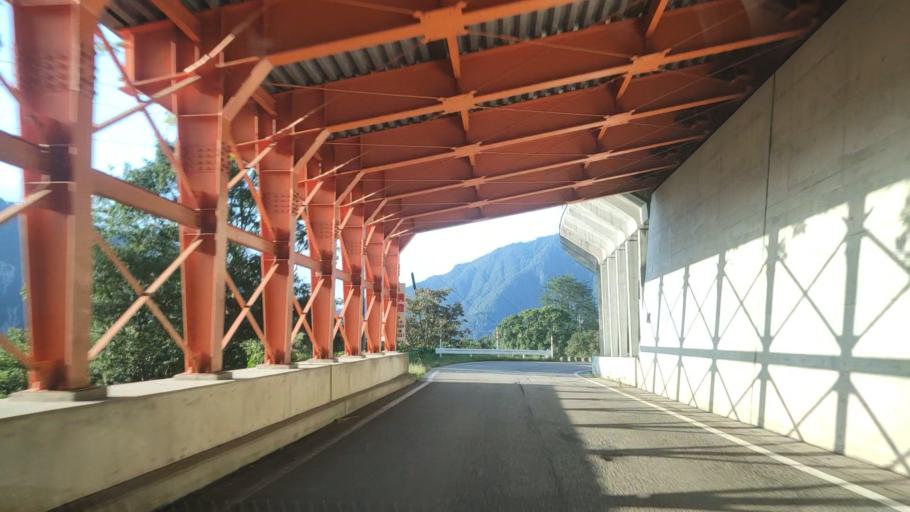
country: JP
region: Toyama
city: Yatsuomachi-higashikumisaka
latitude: 36.5081
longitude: 137.0228
